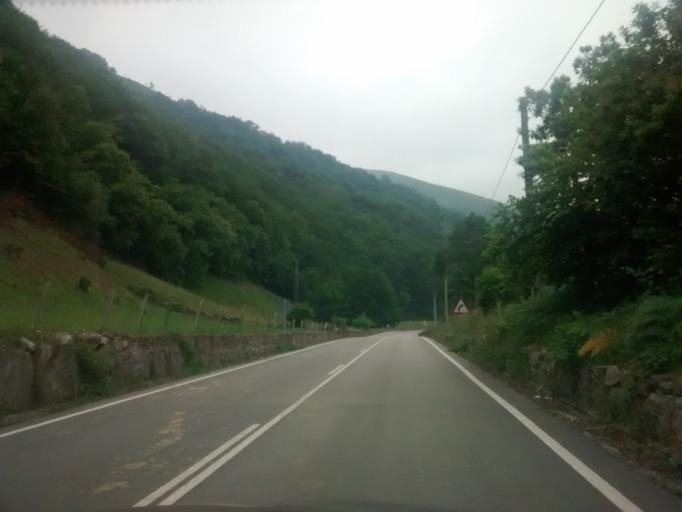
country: ES
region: Cantabria
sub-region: Provincia de Cantabria
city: Ruente
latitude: 43.1820
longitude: -4.3018
